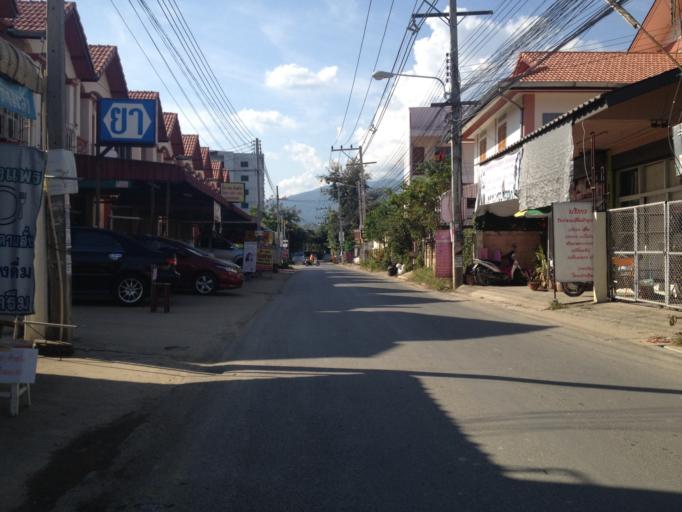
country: TH
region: Chiang Mai
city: Chiang Mai
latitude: 18.7634
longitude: 98.9779
